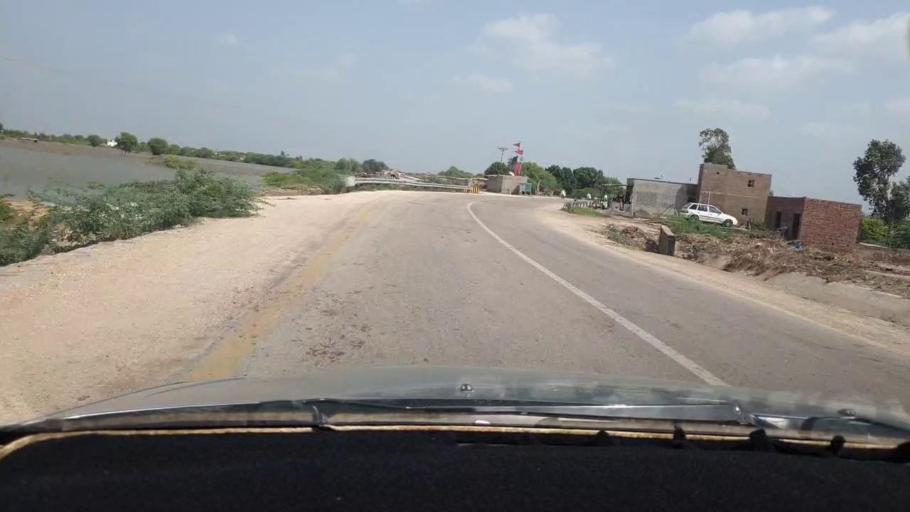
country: PK
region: Sindh
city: Digri
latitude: 25.1002
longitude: 69.1832
